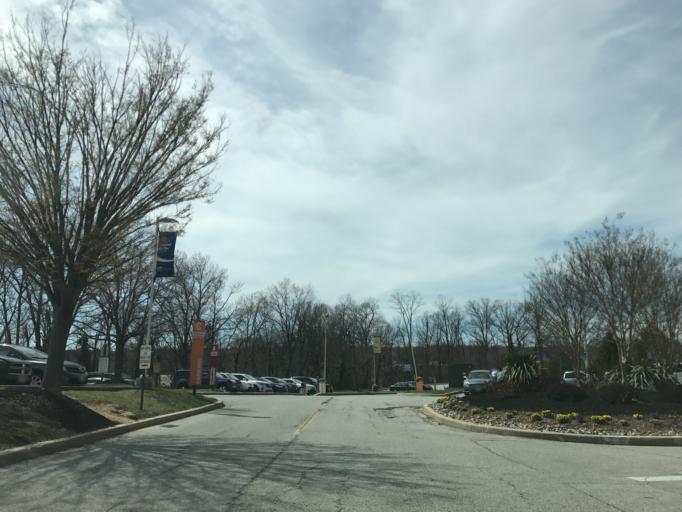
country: US
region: Maryland
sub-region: Baltimore County
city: Towson
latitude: 39.3574
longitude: -76.5874
